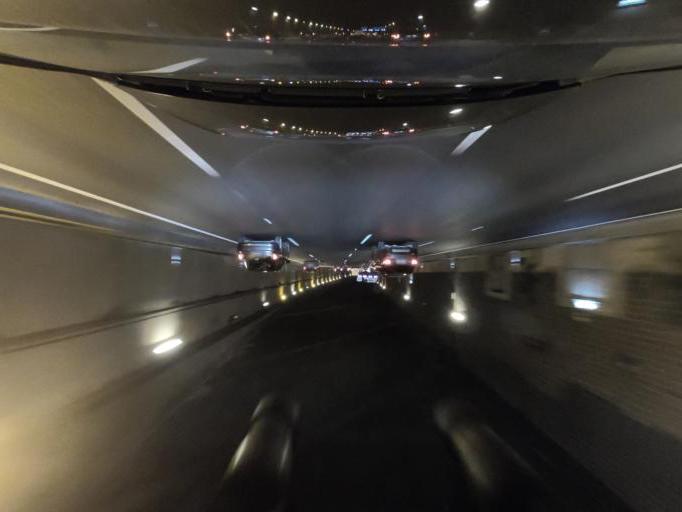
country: PT
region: Lisbon
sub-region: Odivelas
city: Pontinha
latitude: 38.7447
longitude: -9.2070
